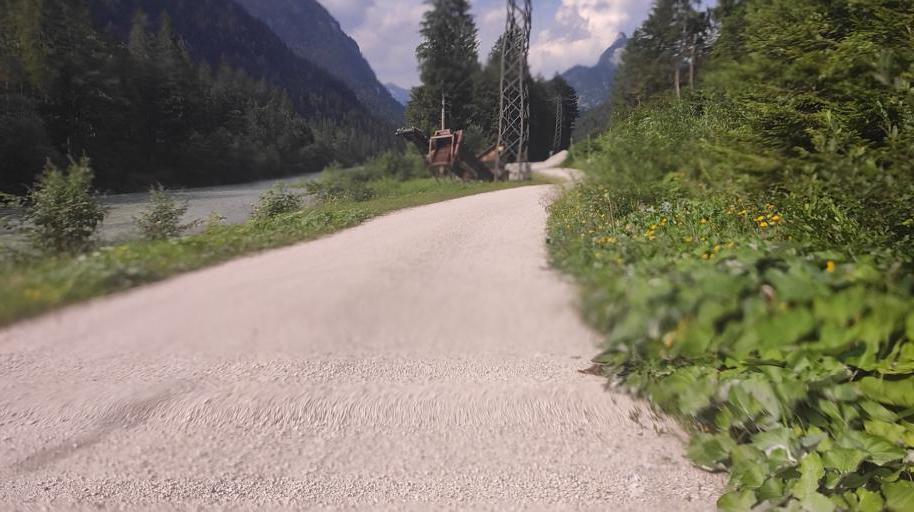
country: DE
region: Bavaria
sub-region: Upper Bavaria
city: Schneizlreuth
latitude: 47.6664
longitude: 12.7739
